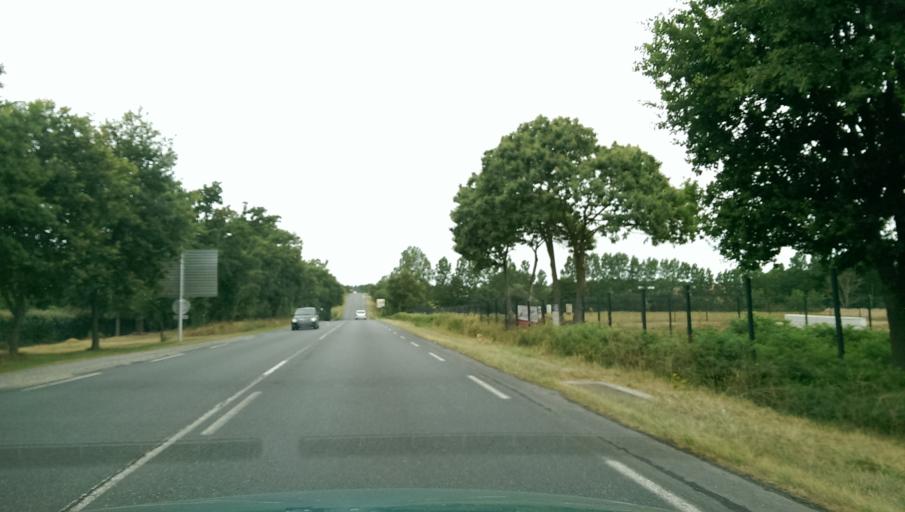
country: FR
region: Pays de la Loire
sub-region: Departement de la Loire-Atlantique
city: Remouille
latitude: 47.0591
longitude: -1.3769
